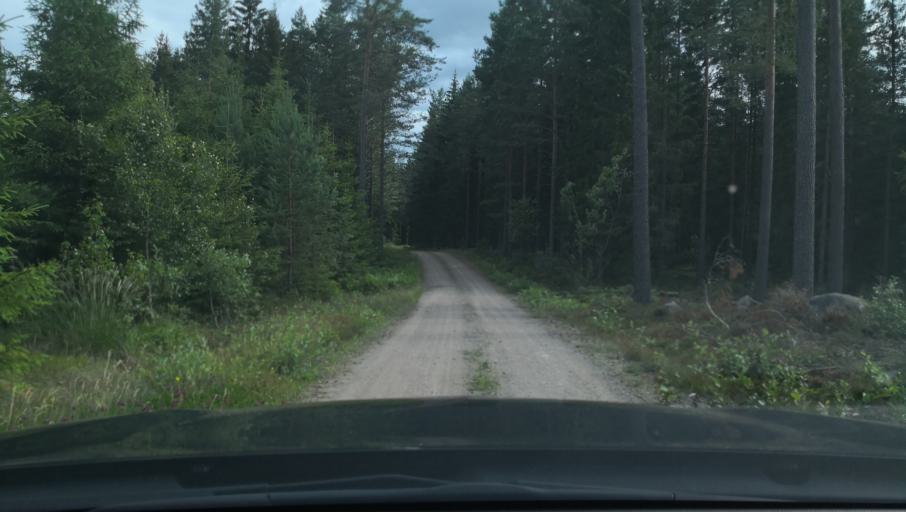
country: SE
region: Vaestmanland
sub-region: Hallstahammars Kommun
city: Hallstahammar
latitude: 59.6430
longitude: 16.0821
